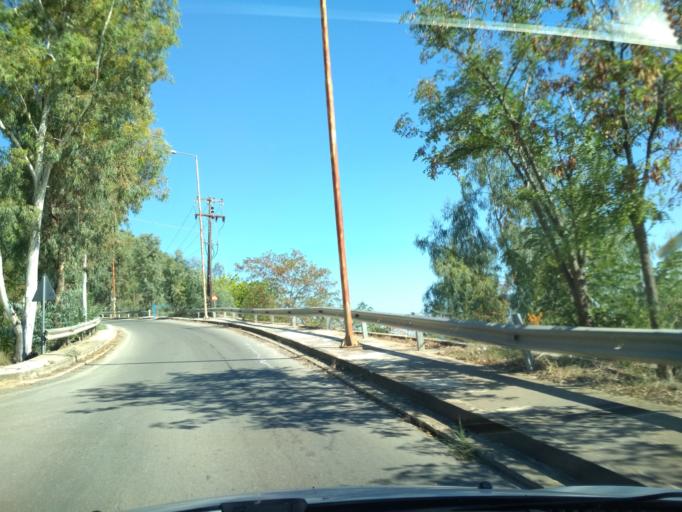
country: GR
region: Central Greece
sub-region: Nomos Evvoias
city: Oreoi
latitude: 38.8523
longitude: 23.0548
